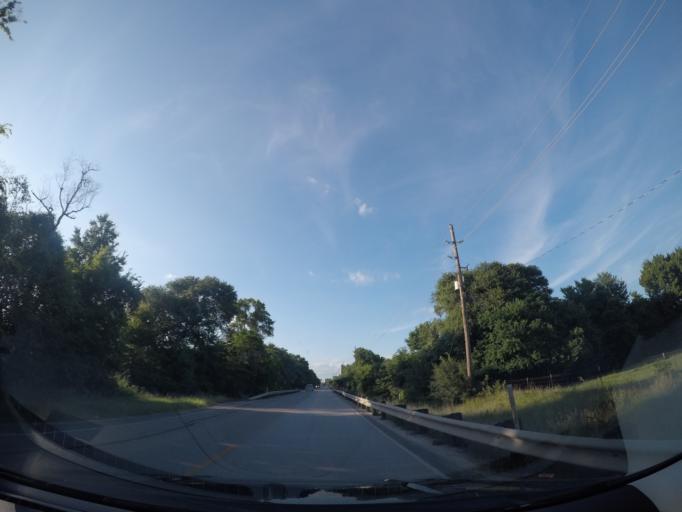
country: US
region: Texas
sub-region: Waller County
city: Brookshire
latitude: 29.7701
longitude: -95.9679
